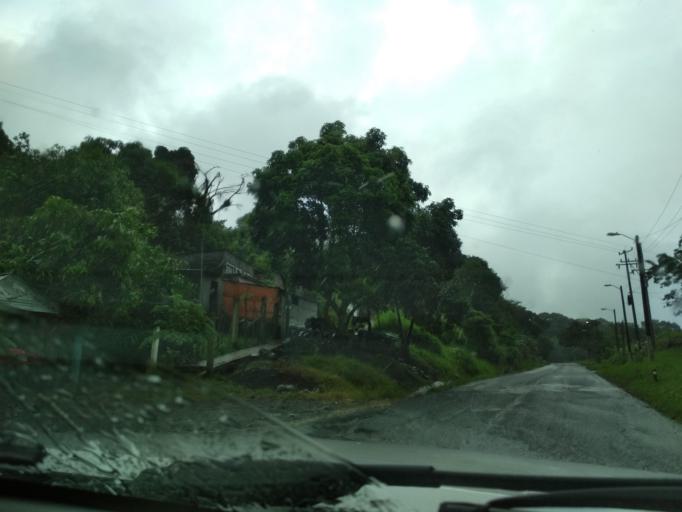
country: MX
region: Veracruz
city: Santiago Tuxtla
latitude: 18.4645
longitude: -95.2929
